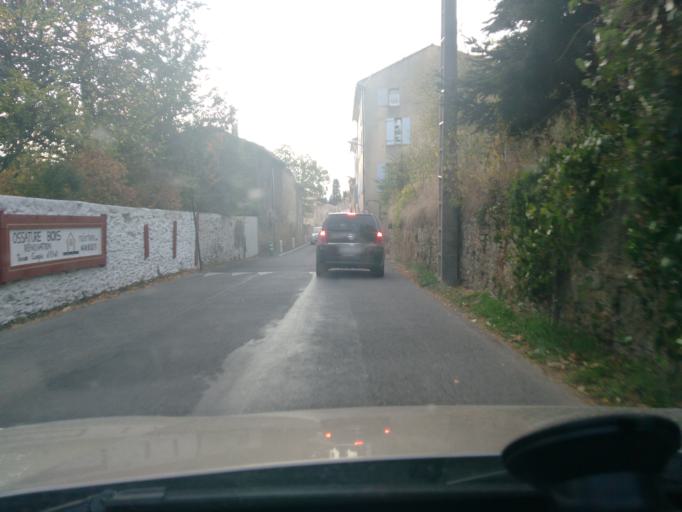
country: FR
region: Rhone-Alpes
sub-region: Departement de la Drome
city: Dieulefit
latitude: 44.5198
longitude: 5.0741
